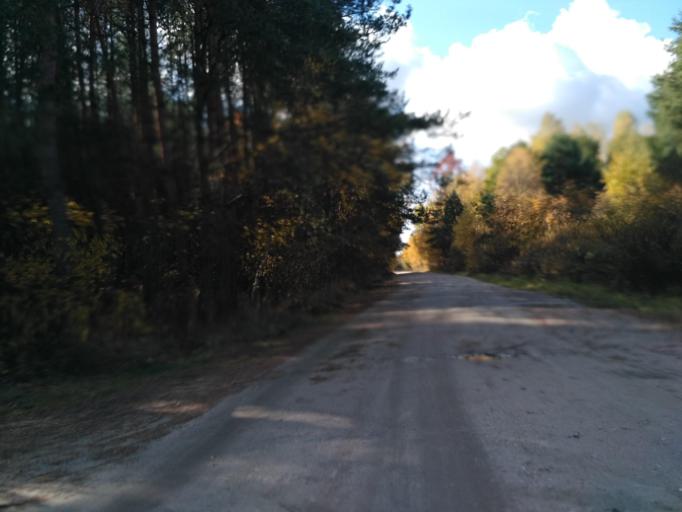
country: PL
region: Subcarpathian Voivodeship
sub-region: Powiat rzeszowski
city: Glogow Malopolski
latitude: 50.1337
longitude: 21.9248
